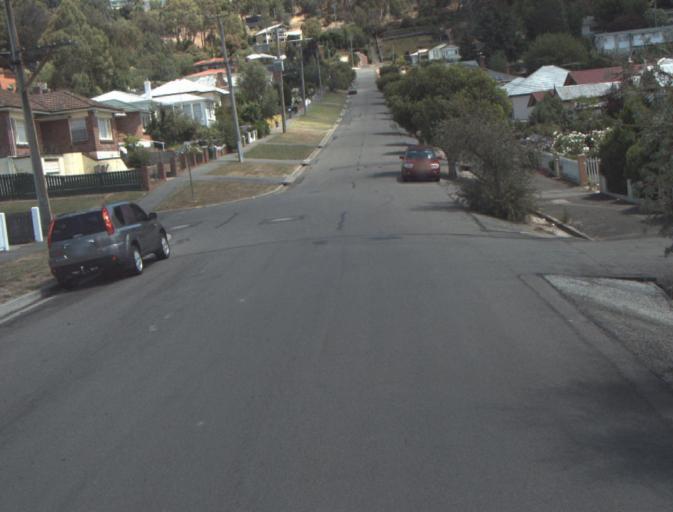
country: AU
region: Tasmania
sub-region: Launceston
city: West Launceston
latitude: -41.4542
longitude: 147.1365
